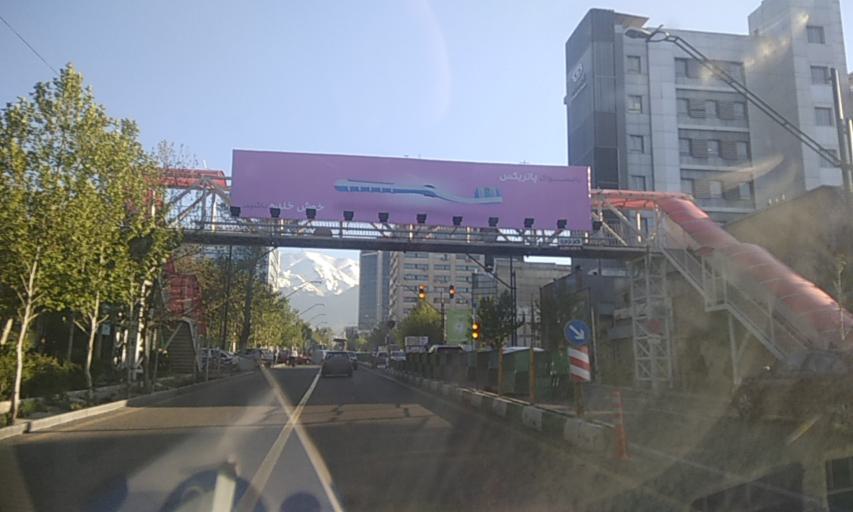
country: IR
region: Tehran
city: Tajrish
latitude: 35.7659
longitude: 51.4108
